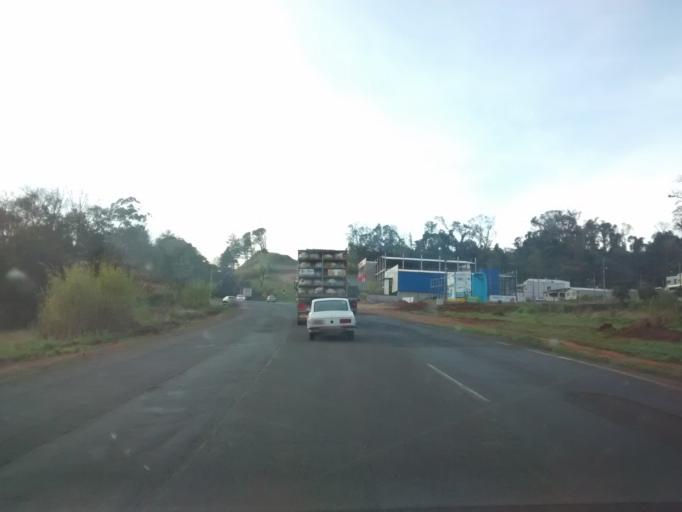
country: BR
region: Parana
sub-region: Francisco Beltrao
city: Francisco Beltrao
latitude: -26.0891
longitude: -53.0658
